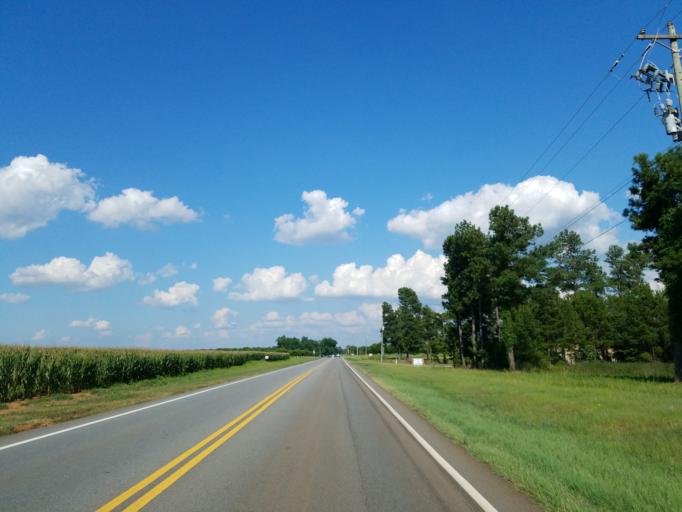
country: US
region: Georgia
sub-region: Peach County
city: Fort Valley
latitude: 32.5538
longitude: -83.7935
